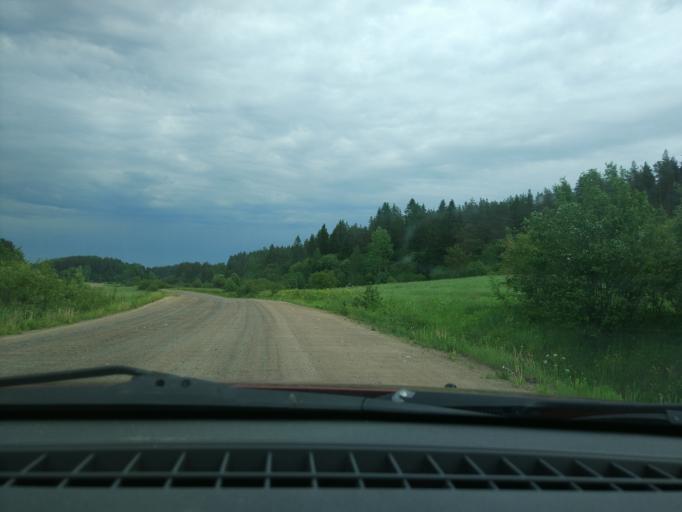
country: RU
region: Leningrad
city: Kuznechnoye
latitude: 61.2757
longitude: 29.8460
